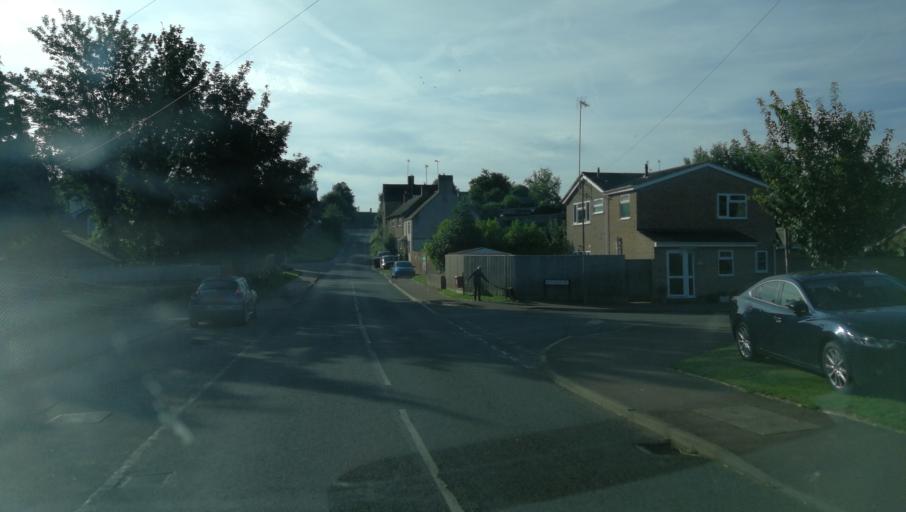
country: GB
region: England
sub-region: Oxfordshire
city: Bloxham
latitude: 52.0176
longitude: -1.3812
